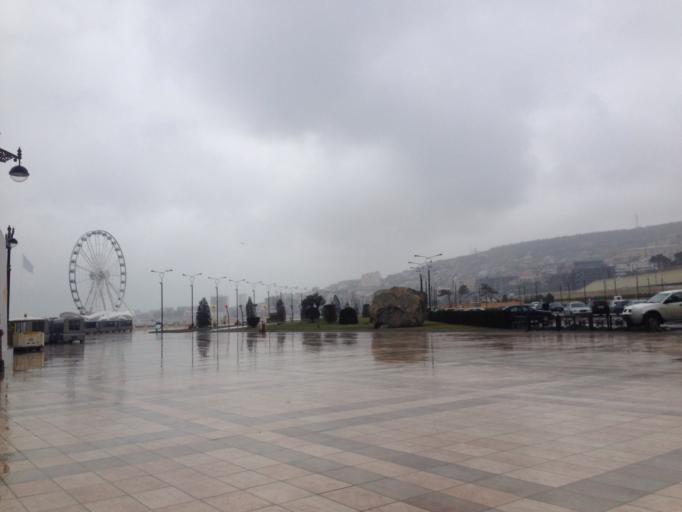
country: AZ
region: Baki
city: Badamdar
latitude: 40.3583
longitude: 49.8359
